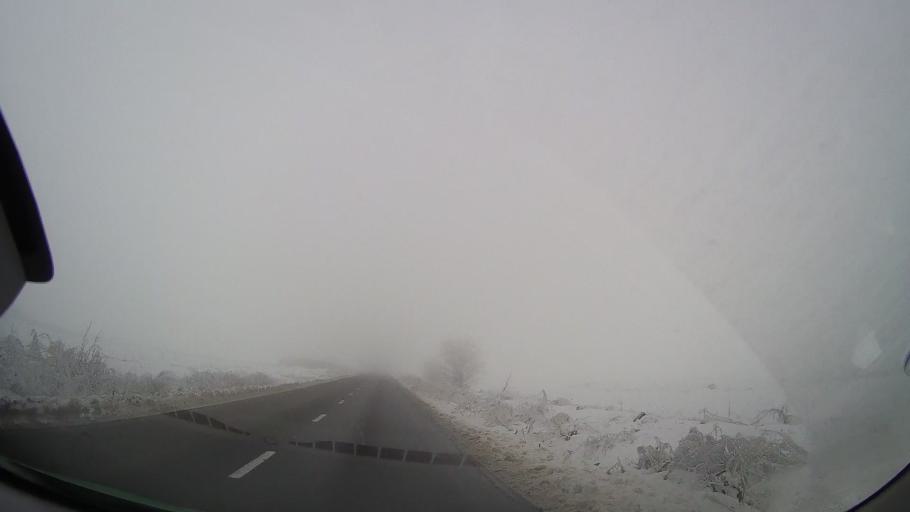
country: RO
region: Neamt
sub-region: Comuna Sabaoani
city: Sabaoani
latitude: 47.0344
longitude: 26.8553
